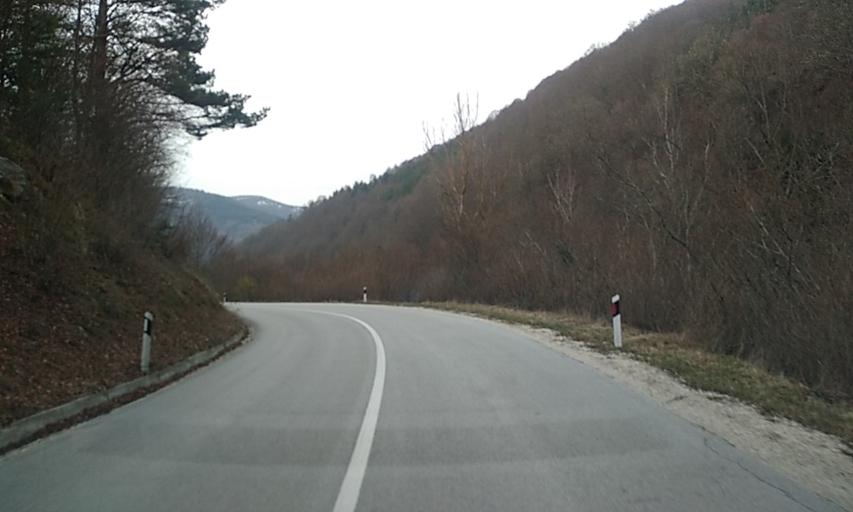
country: RS
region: Central Serbia
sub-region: Pcinjski Okrug
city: Bosilegrad
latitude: 42.5972
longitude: 22.4100
